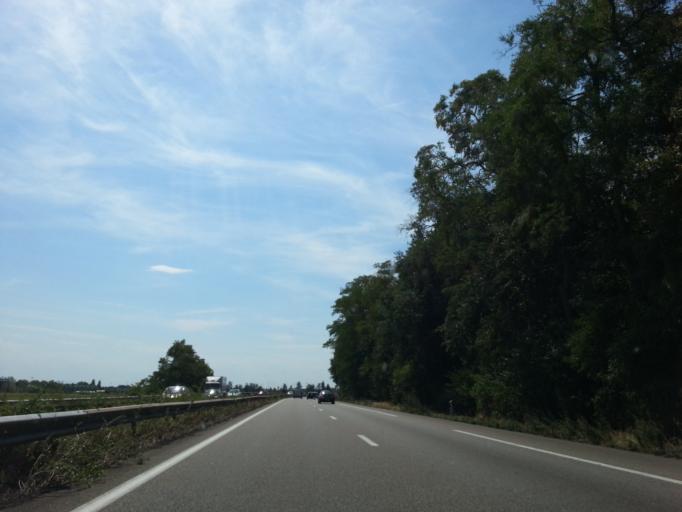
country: FR
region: Alsace
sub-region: Departement du Haut-Rhin
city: Houssen
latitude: 48.1340
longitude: 7.3653
